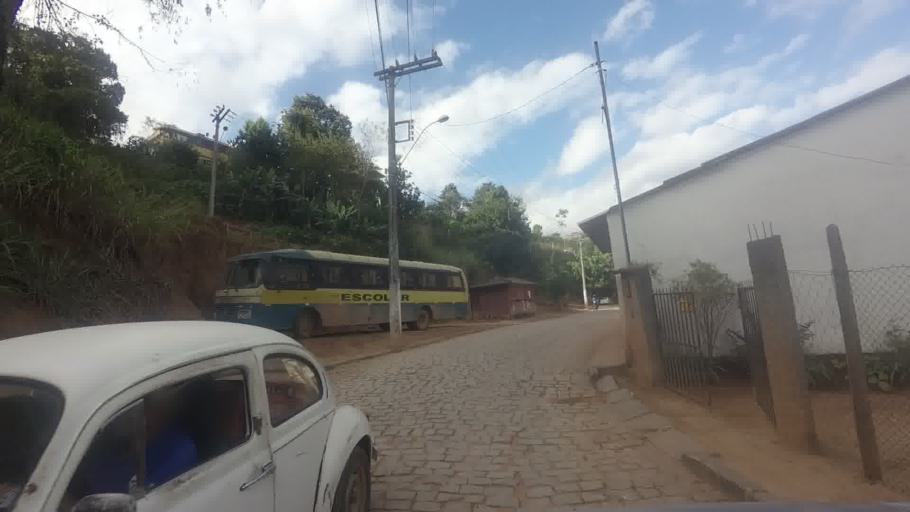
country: BR
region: Espirito Santo
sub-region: Sao Jose Do Calcado
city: Sao Jose do Calcado
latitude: -20.9719
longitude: -41.5086
